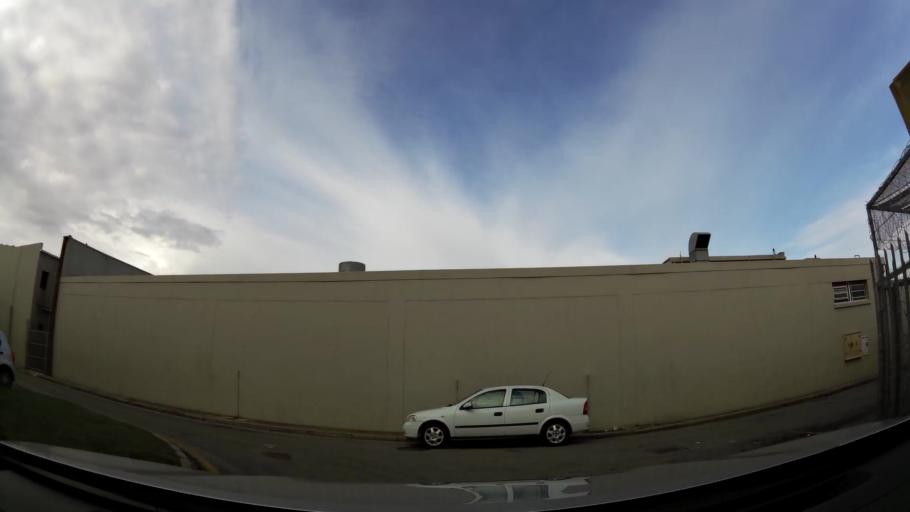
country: ZA
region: Eastern Cape
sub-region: Nelson Mandela Bay Metropolitan Municipality
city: Port Elizabeth
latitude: -33.9432
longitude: 25.5136
